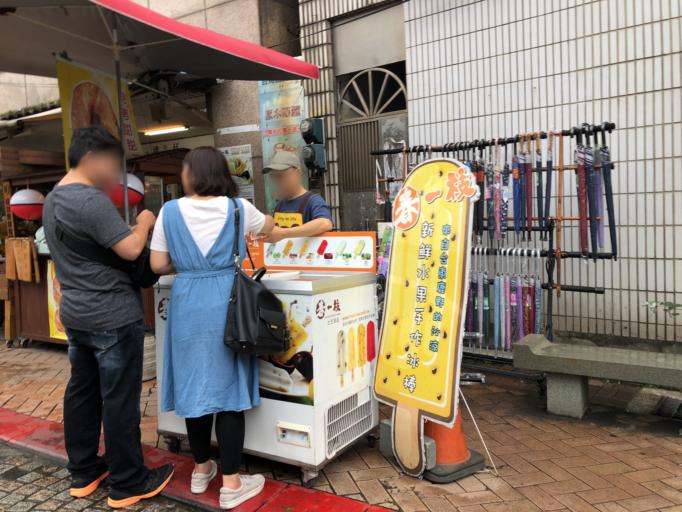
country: TW
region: Taiwan
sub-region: Taoyuan
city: Taoyuan
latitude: 24.9511
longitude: 121.3474
